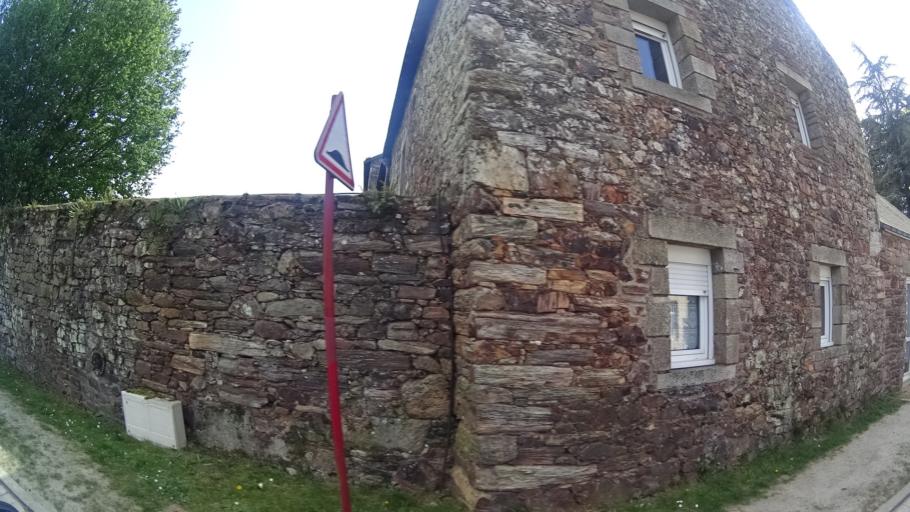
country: FR
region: Brittany
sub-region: Departement du Morbihan
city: Beganne
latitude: 47.5964
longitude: -2.2423
